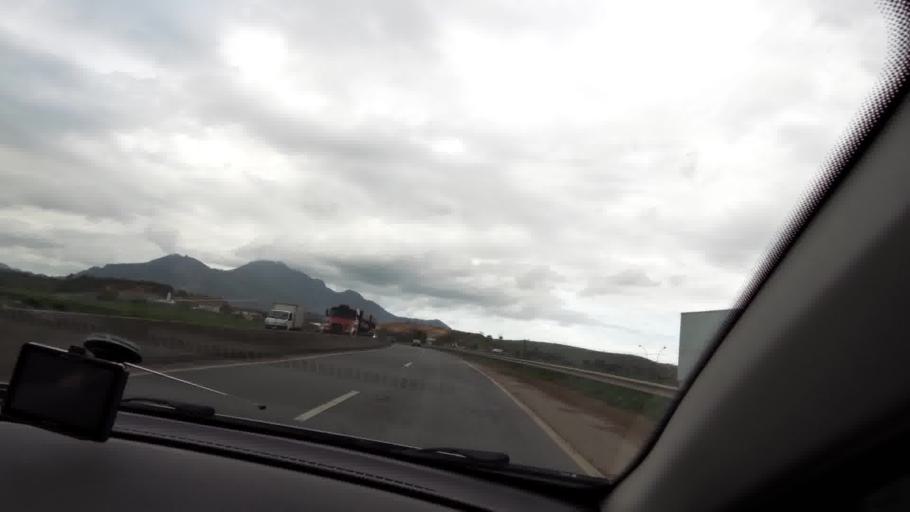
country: BR
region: Espirito Santo
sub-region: Vitoria
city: Vitoria
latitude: -20.2244
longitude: -40.3605
